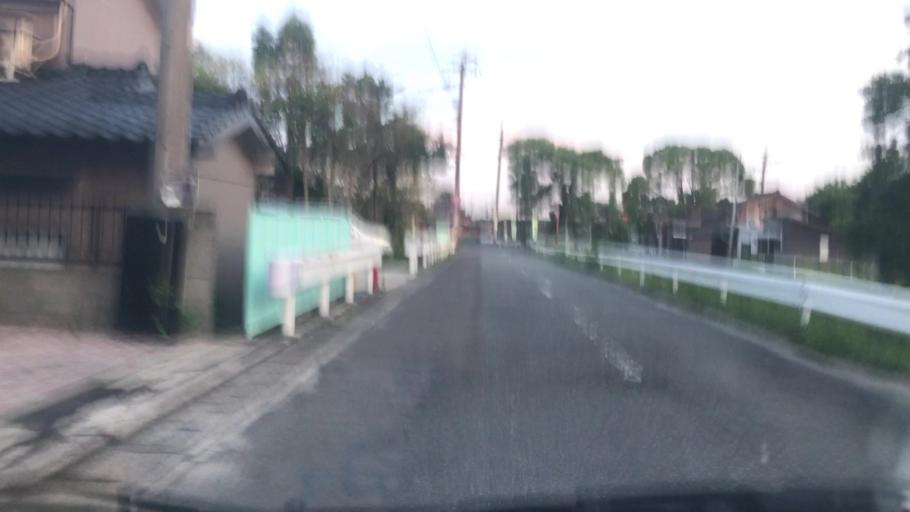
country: JP
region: Saga Prefecture
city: Saga-shi
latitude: 33.2534
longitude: 130.2830
